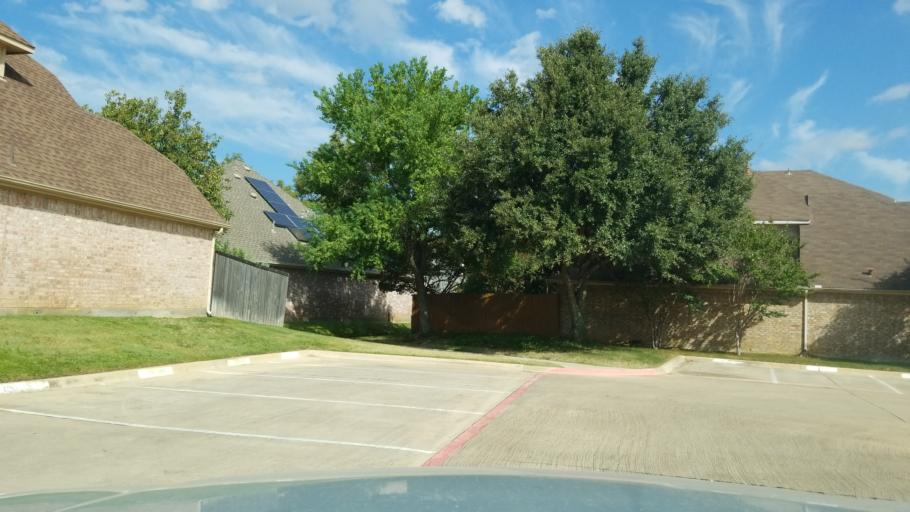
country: US
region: Texas
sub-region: Tarrant County
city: Euless
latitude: 32.8447
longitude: -97.0803
